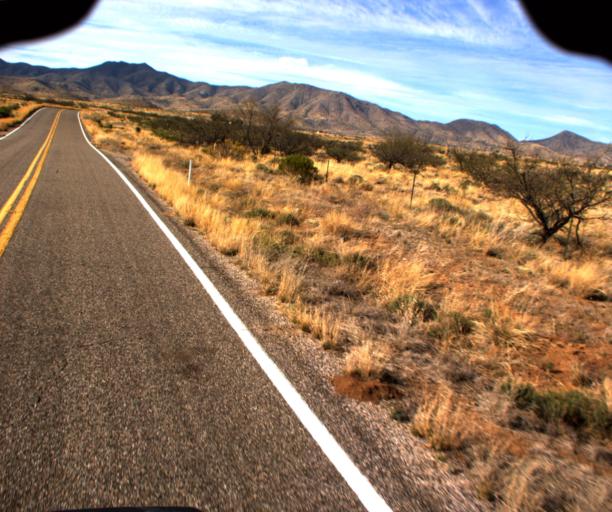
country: US
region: Arizona
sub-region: Cochise County
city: Willcox
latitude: 32.1256
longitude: -109.5563
